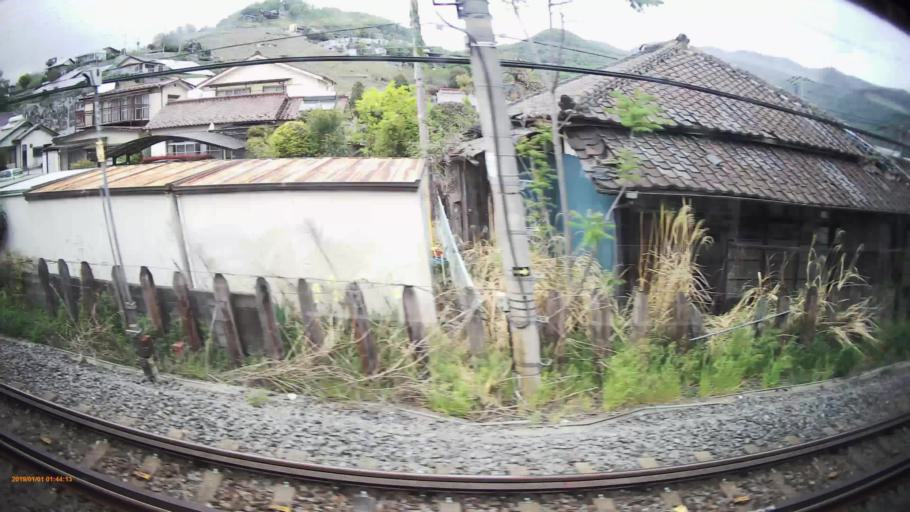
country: JP
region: Yamanashi
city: Kofu-shi
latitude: 35.6617
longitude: 138.5810
